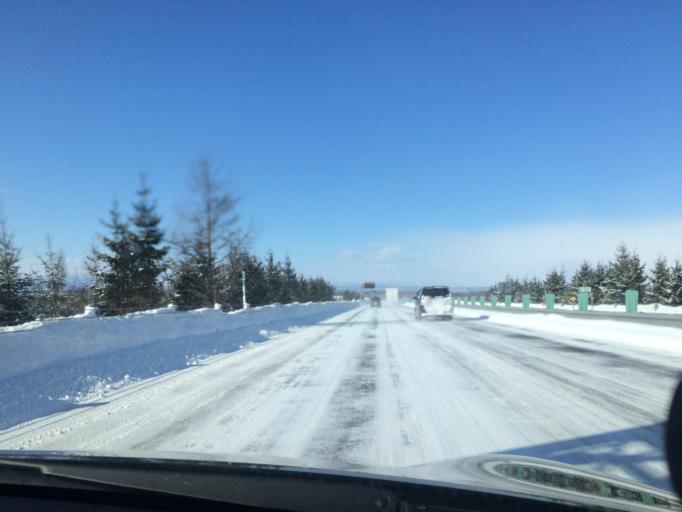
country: JP
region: Hokkaido
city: Chitose
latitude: 42.8799
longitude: 141.7203
